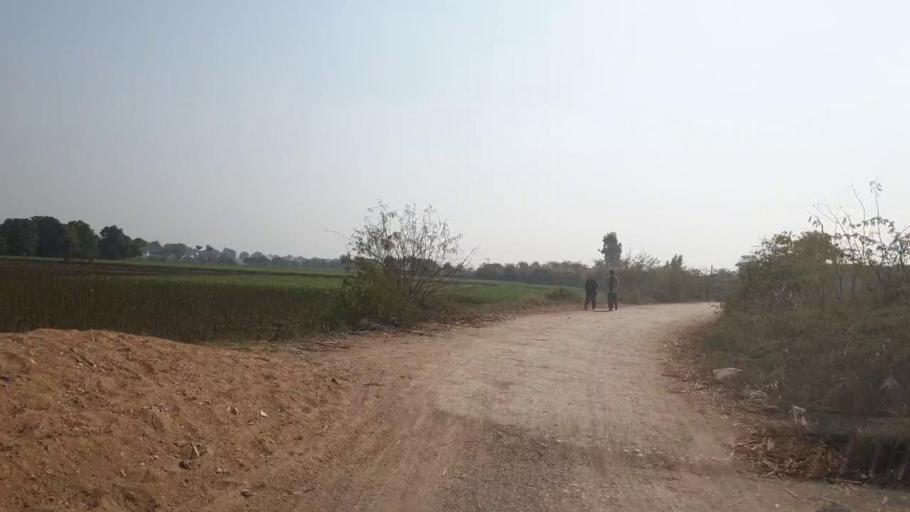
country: PK
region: Sindh
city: Bhit Shah
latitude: 25.7103
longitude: 68.5465
